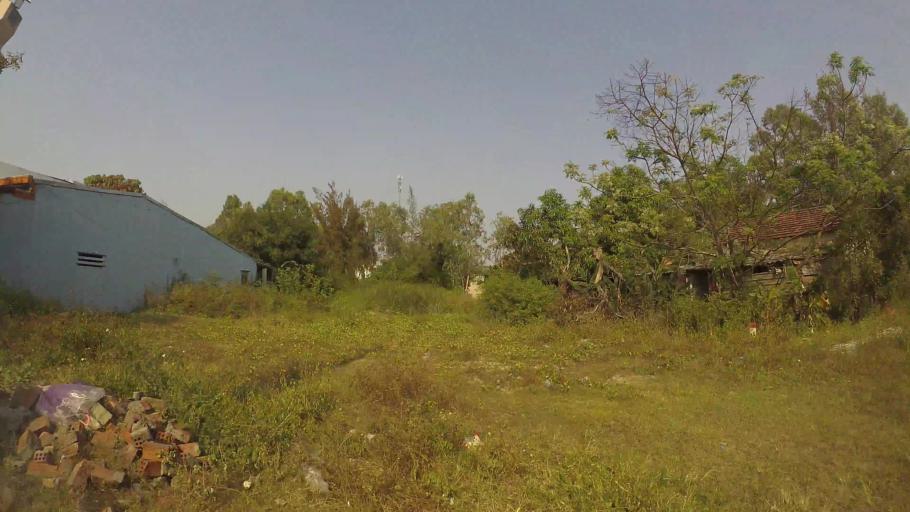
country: VN
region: Quang Nam
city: Quang Nam
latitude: 15.9496
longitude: 108.2674
